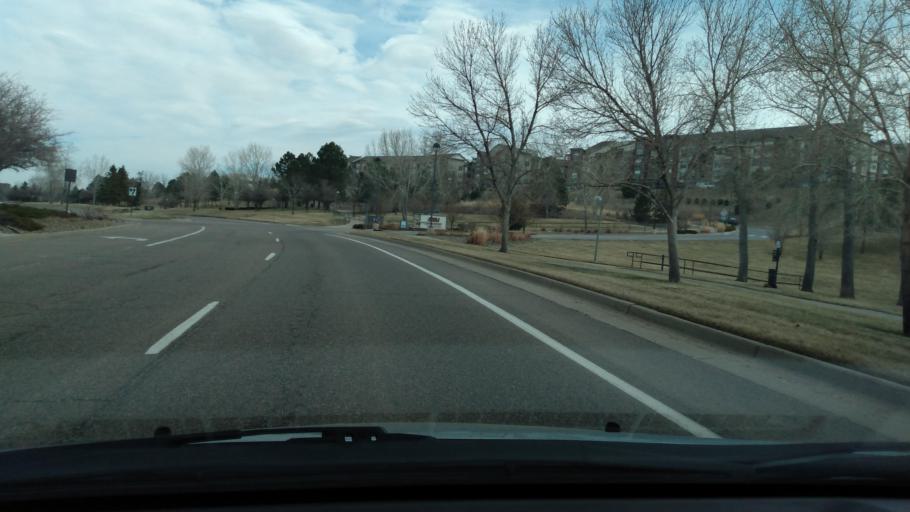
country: US
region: Colorado
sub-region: Broomfield County
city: Broomfield
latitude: 39.9224
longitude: -105.1188
